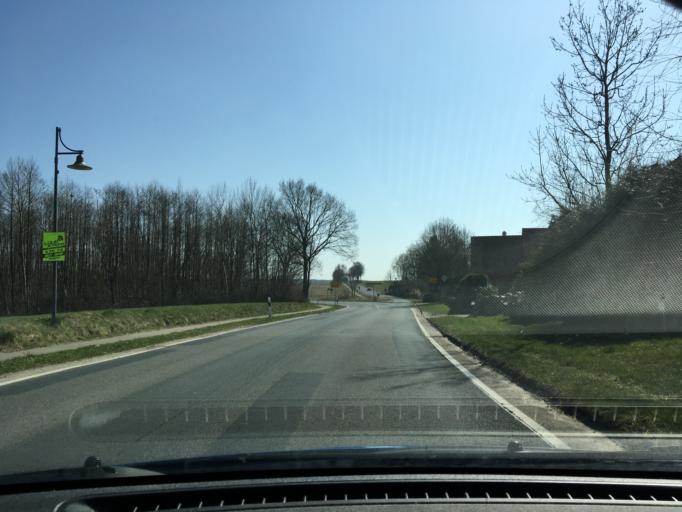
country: DE
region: Lower Saxony
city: Amelinghausen
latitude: 53.1229
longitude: 10.2155
